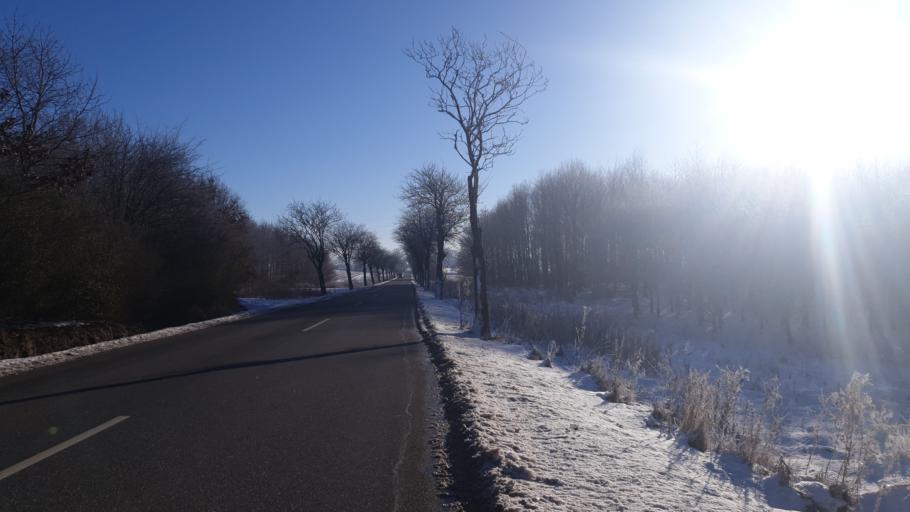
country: DK
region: Central Jutland
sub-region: Hedensted Kommune
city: Hedensted
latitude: 55.8006
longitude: 9.7235
